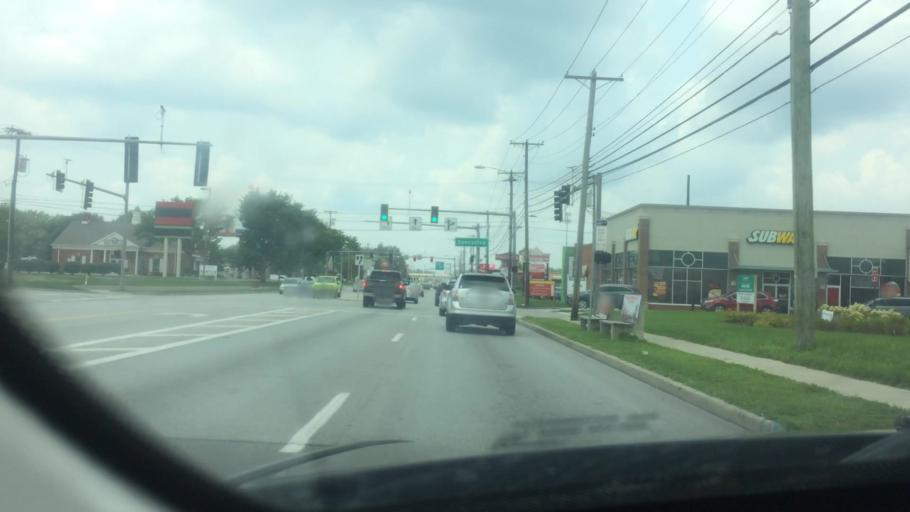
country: US
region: Ohio
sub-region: Lucas County
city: Ottawa Hills
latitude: 41.6809
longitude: -83.6227
